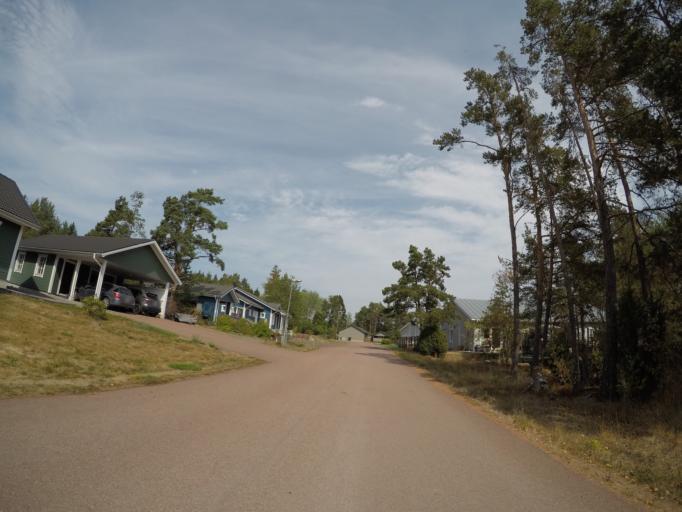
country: AX
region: Alands landsbygd
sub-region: Finstroem
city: Finstroem
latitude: 60.2344
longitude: 19.9852
